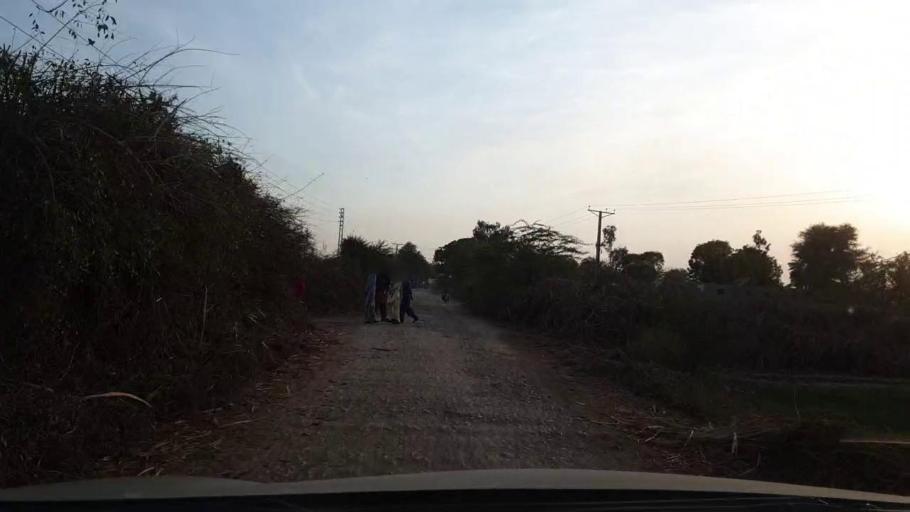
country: PK
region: Sindh
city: Tando Adam
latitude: 25.7110
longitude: 68.7203
